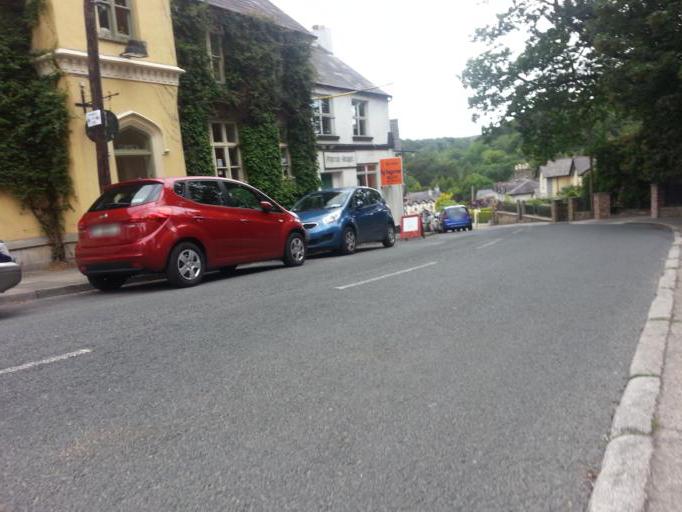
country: IE
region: Leinster
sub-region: Wicklow
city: Enniskerry
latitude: 53.1918
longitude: -6.1692
